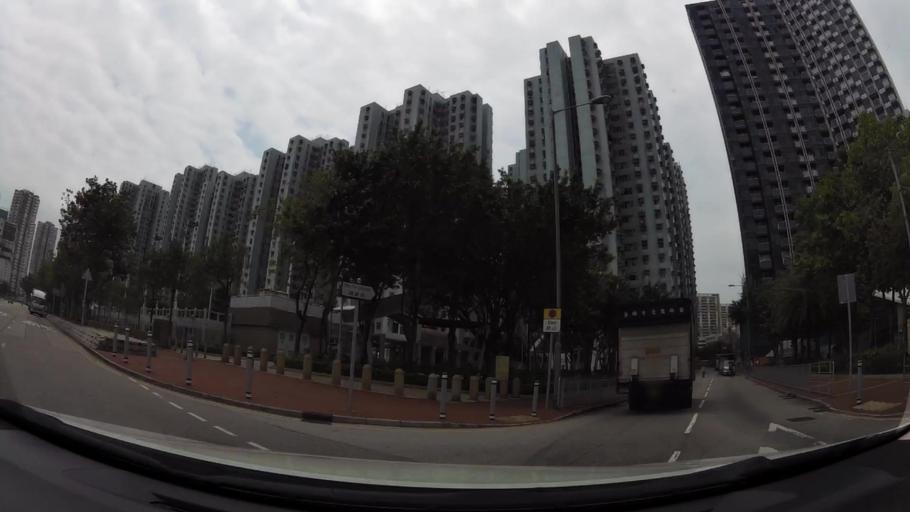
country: HK
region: Tuen Mun
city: Tuen Mun
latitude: 22.3763
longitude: 113.9683
